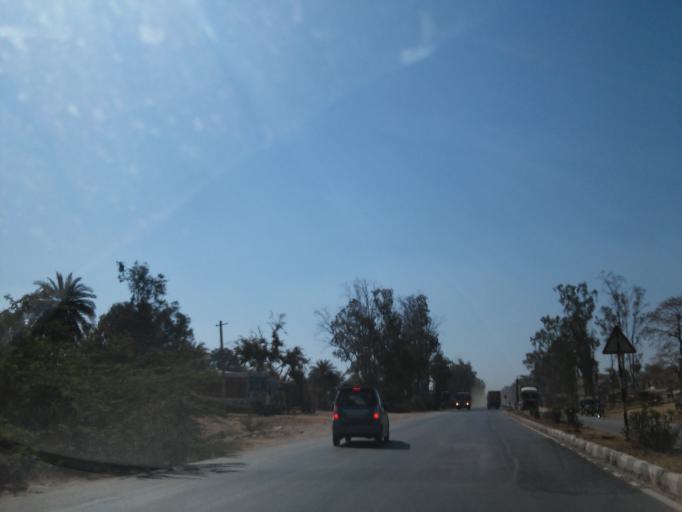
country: IN
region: Rajasthan
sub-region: Dungarpur
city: Dungarpur
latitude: 23.7925
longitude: 73.5227
